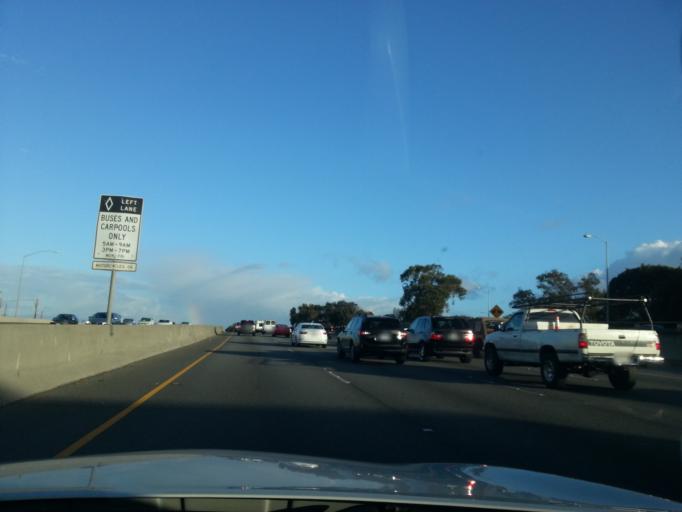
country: US
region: California
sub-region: San Mateo County
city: Redwood City
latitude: 37.4900
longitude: -122.2160
